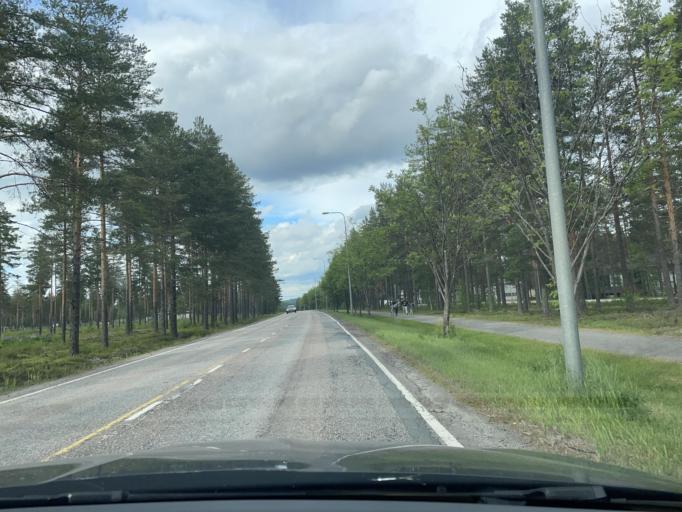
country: FI
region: Central Finland
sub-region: Jaemsae
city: Jaemsaenkoski
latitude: 61.9120
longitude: 25.1428
